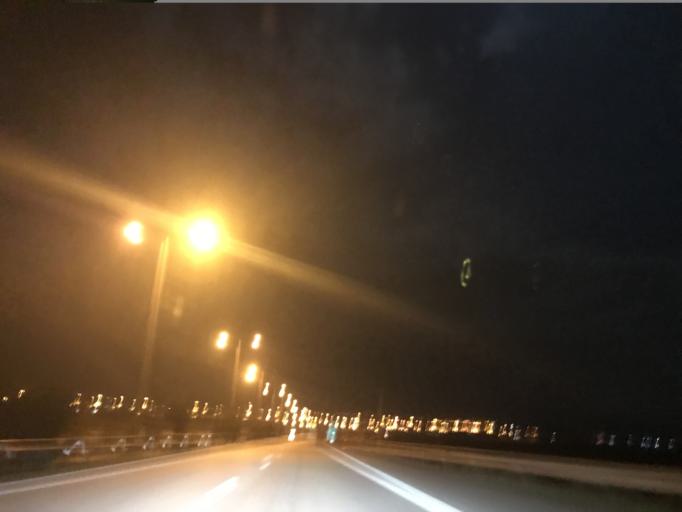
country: TR
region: Hatay
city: Mahmutlar
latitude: 36.9649
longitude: 36.1012
